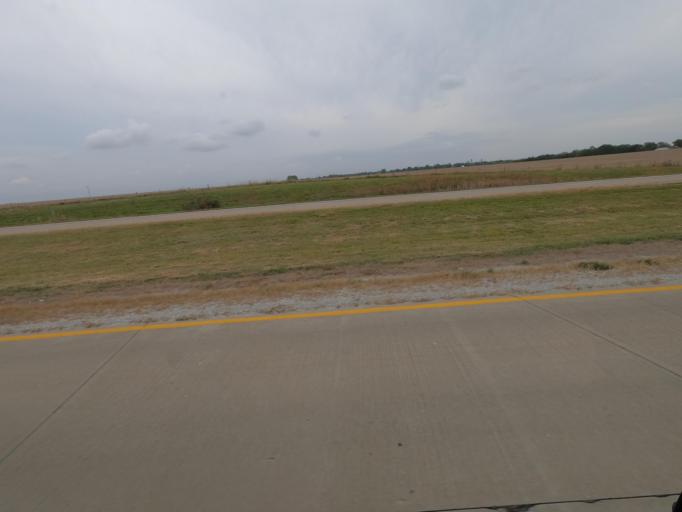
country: US
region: Iowa
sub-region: Jasper County
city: Monroe
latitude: 41.5274
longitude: -93.1305
